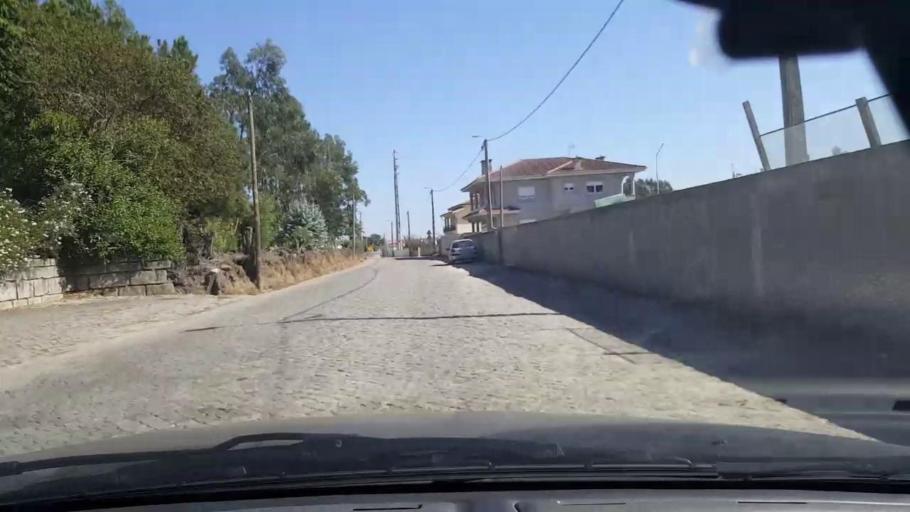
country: PT
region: Porto
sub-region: Matosinhos
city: Lavra
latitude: 41.2951
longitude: -8.7020
